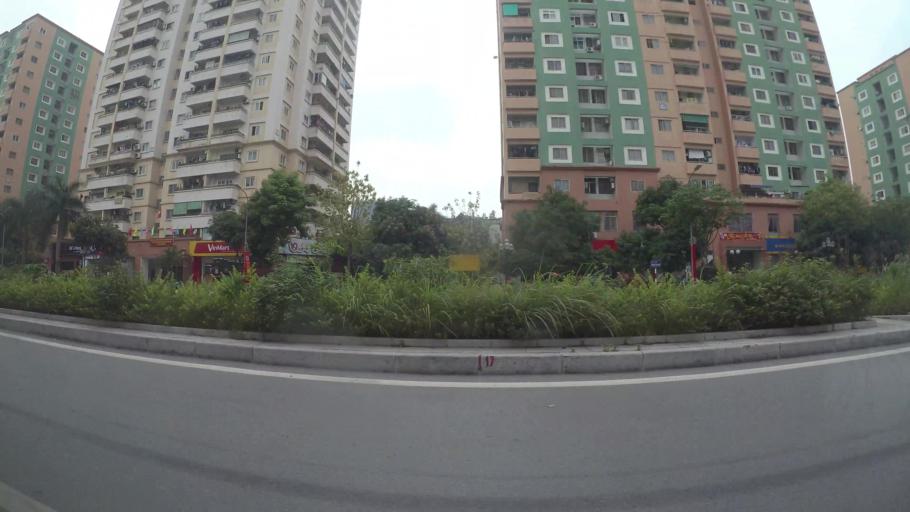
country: VN
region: Ha Noi
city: Cau Dien
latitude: 21.0317
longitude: 105.7651
